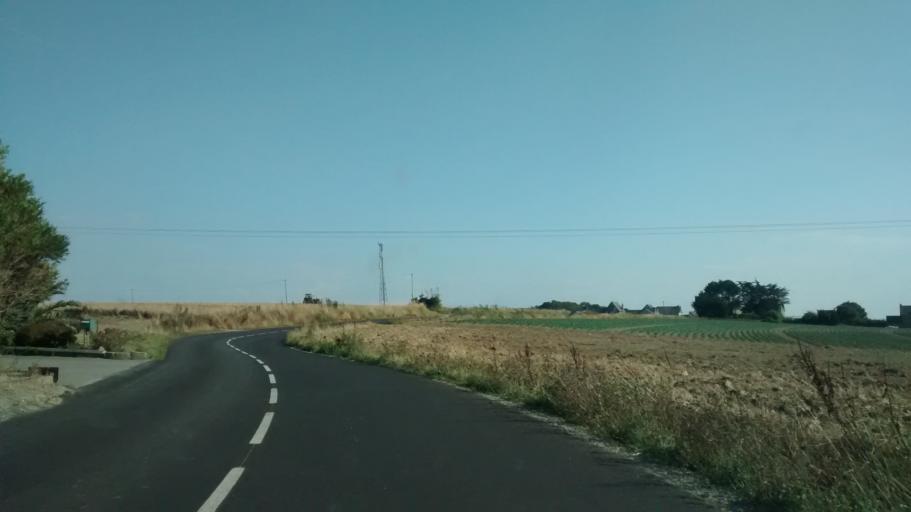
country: FR
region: Brittany
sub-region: Departement d'Ille-et-Vilaine
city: Saint-Coulomb
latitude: 48.6701
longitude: -1.9059
